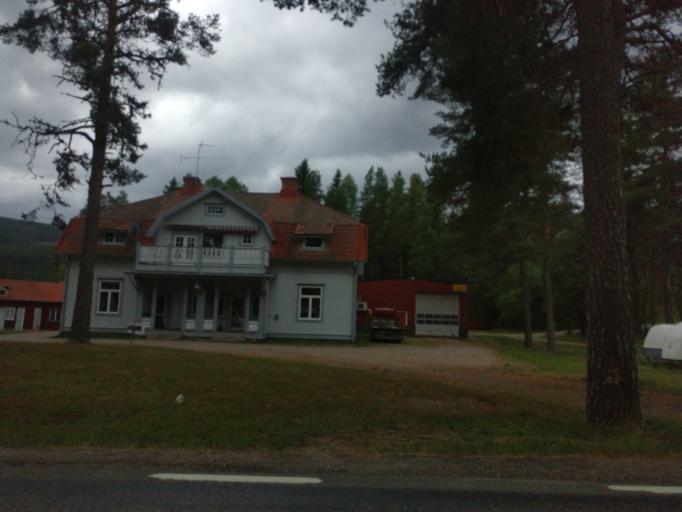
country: SE
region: Vaermland
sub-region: Torsby Kommun
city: Torsby
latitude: 60.6166
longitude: 13.0404
